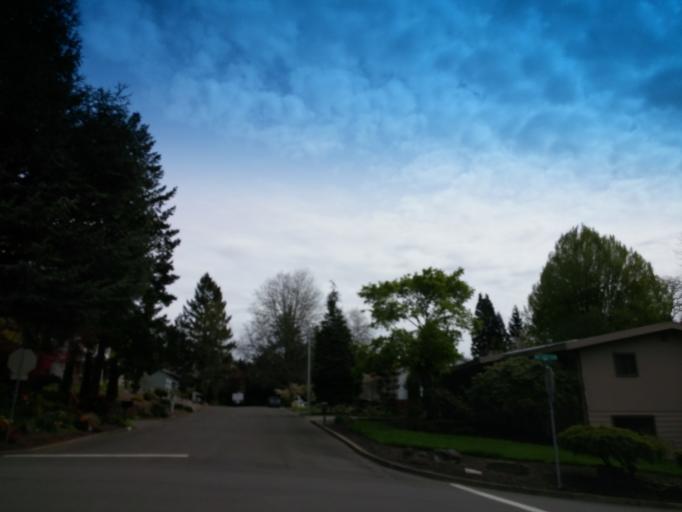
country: US
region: Oregon
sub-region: Washington County
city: Cedar Mill
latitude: 45.5332
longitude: -122.8120
